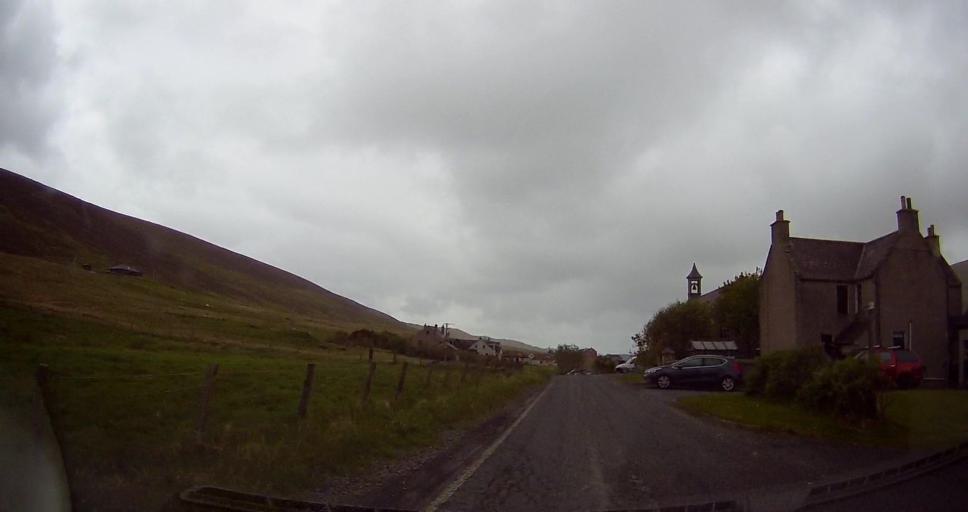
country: GB
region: Scotland
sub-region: Shetland Islands
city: Lerwick
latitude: 60.2564
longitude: -1.2891
